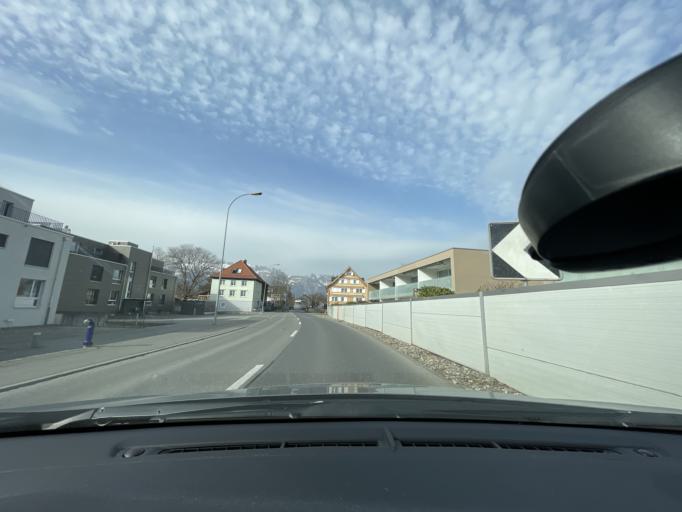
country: CH
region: Saint Gallen
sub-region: Wahlkreis Werdenberg
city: Sevelen
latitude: 47.1438
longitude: 9.4858
